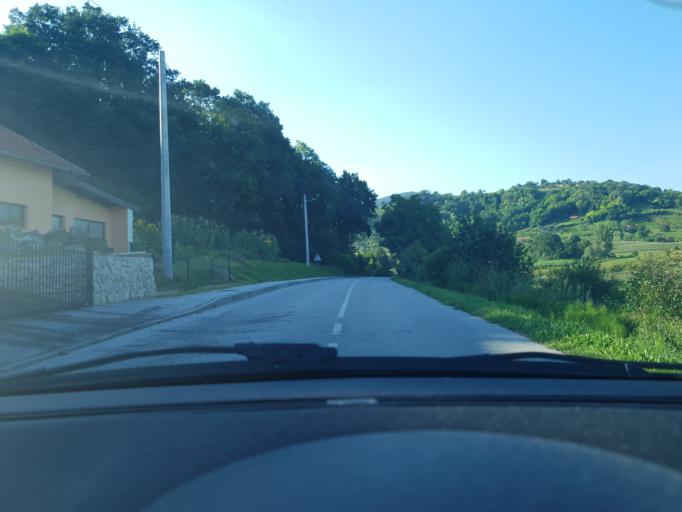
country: HR
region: Krapinsko-Zagorska
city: Radoboj
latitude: 46.1586
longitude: 15.9377
